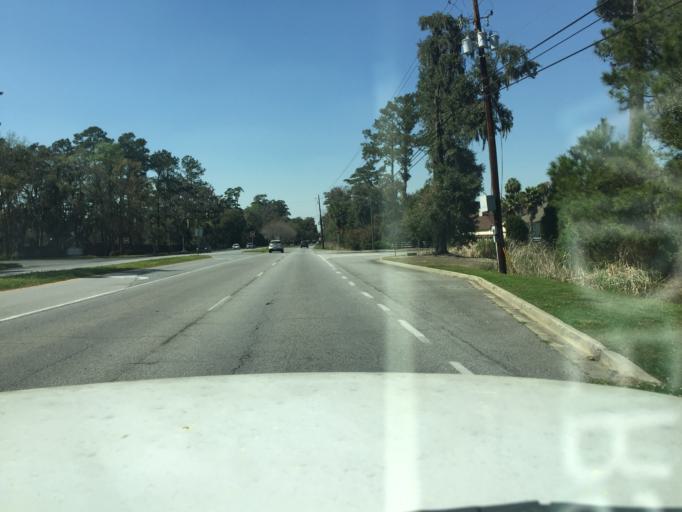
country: US
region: Georgia
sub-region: Chatham County
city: Whitemarsh Island
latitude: 32.0367
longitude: -81.0125
